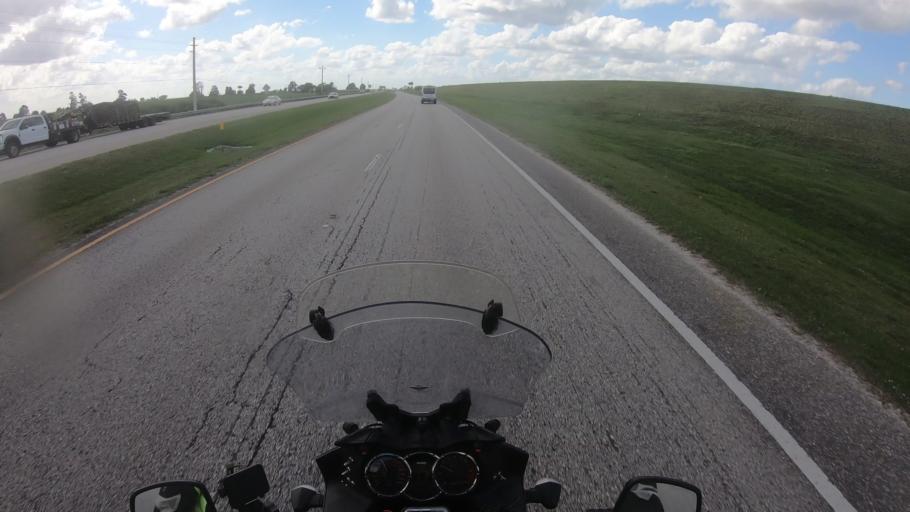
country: US
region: Florida
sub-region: Palm Beach County
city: South Bay
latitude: 26.6806
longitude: -80.7334
